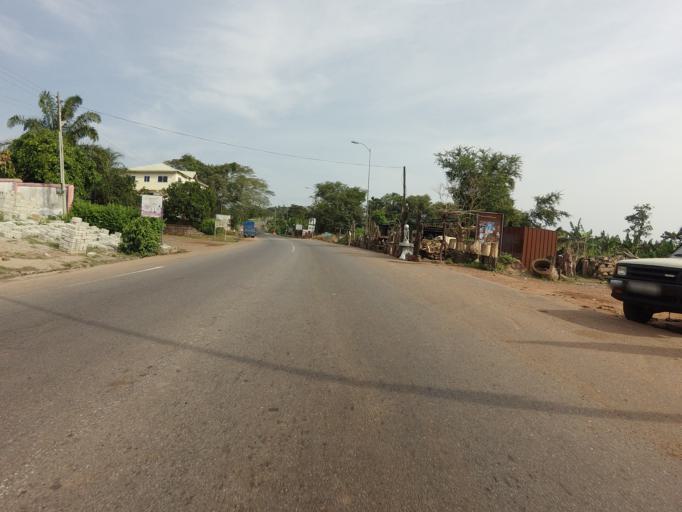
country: GH
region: Eastern
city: Aburi
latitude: 5.8202
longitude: -0.1863
